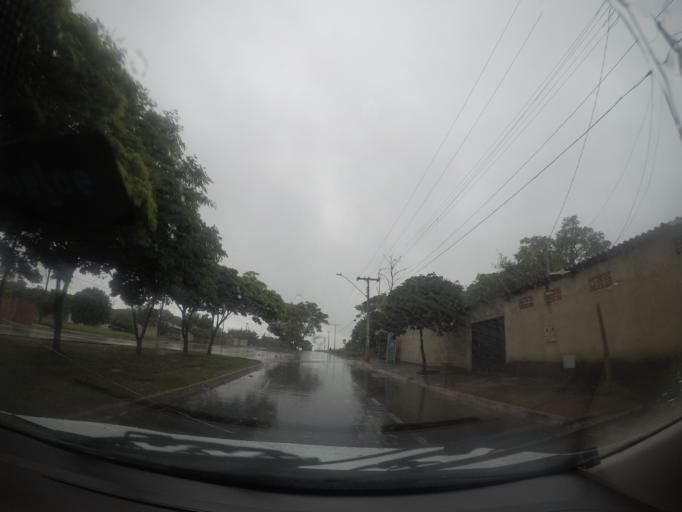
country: BR
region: Goias
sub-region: Goiania
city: Goiania
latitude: -16.5957
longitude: -49.3374
